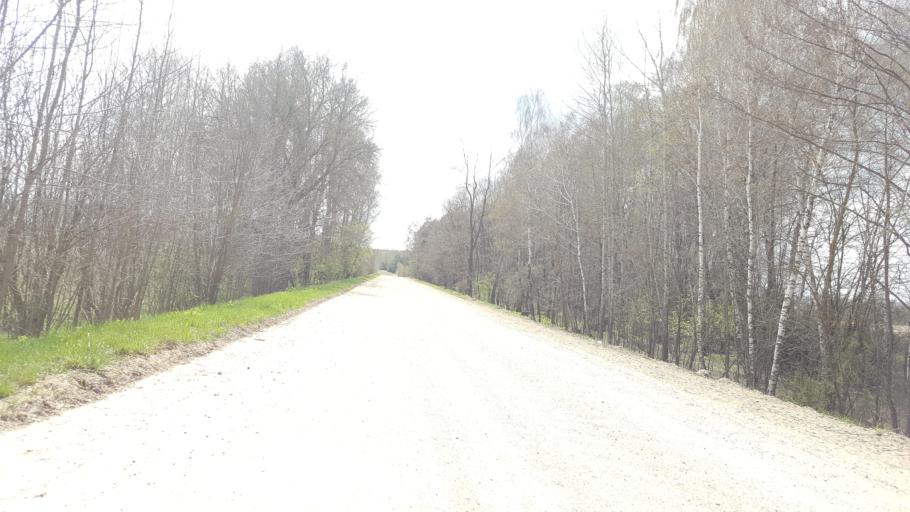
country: BY
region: Brest
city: Kamyanyets
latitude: 52.3705
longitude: 23.7288
